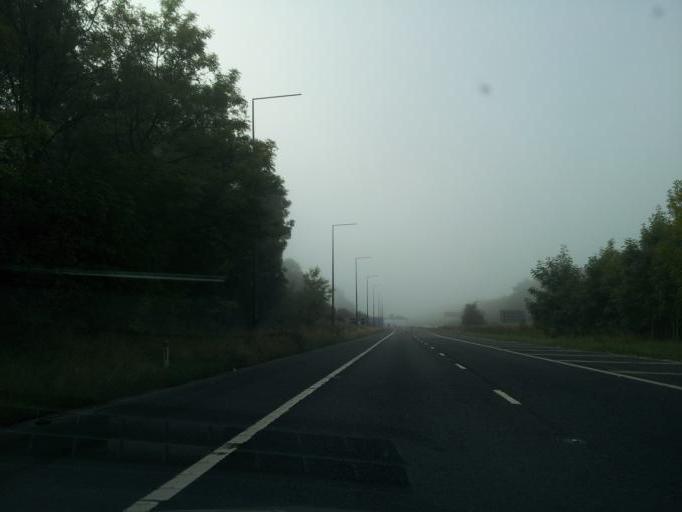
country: GB
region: England
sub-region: Borough of Rochdale
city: Rochdale
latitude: 53.5832
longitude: -2.1575
